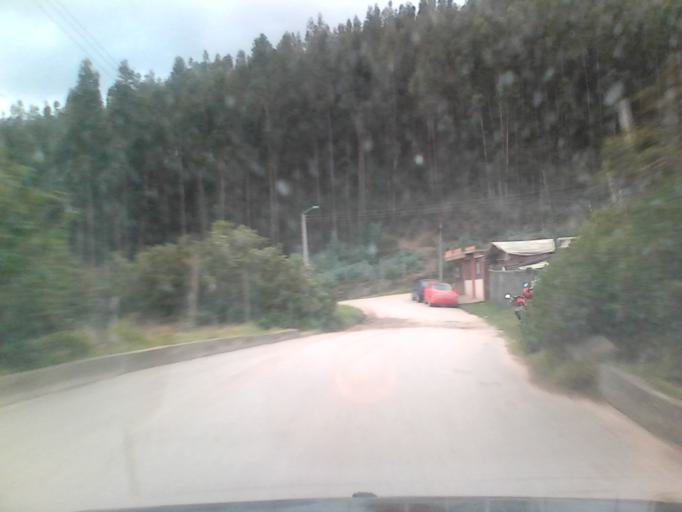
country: CO
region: Boyaca
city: Duitama
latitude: 5.8476
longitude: -73.0373
